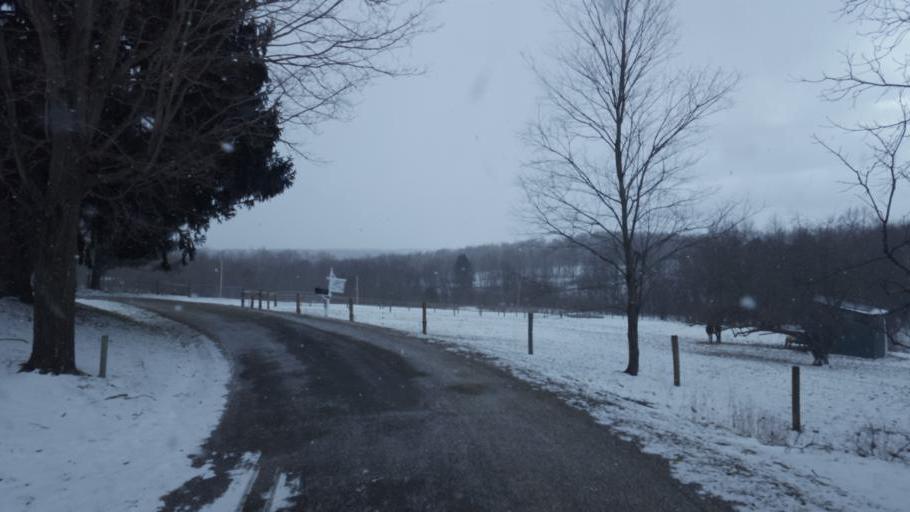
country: US
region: Pennsylvania
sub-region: Mercer County
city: Stoneboro
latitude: 41.4234
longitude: -80.0682
